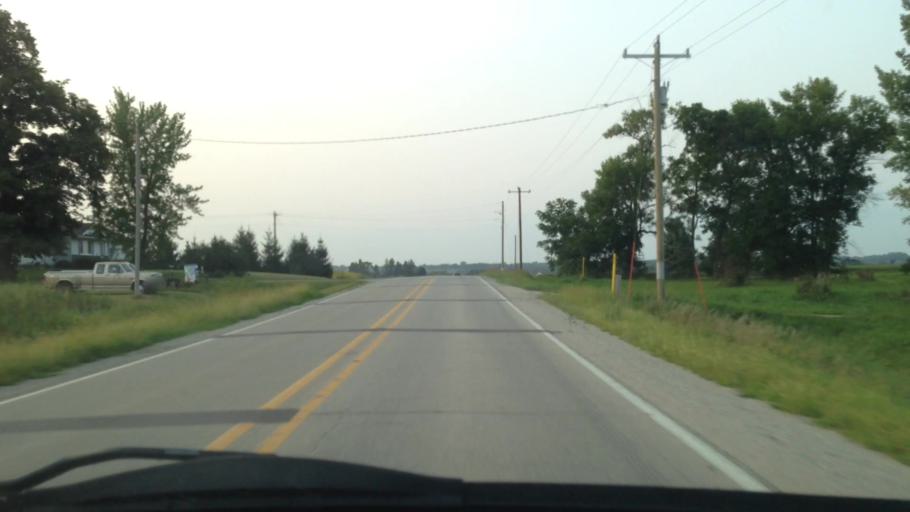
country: US
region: Iowa
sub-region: Linn County
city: Palo
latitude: 42.0787
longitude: -91.8690
